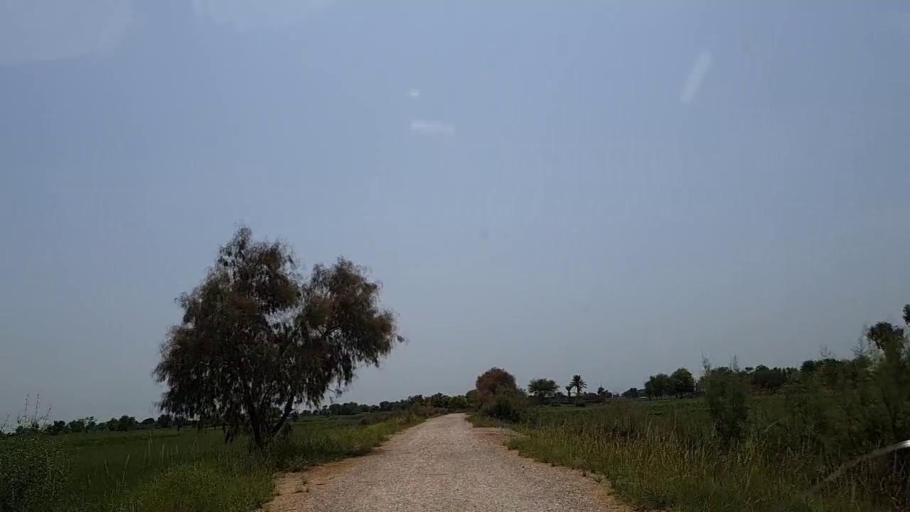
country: PK
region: Sindh
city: Ghotki
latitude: 27.9846
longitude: 69.4048
